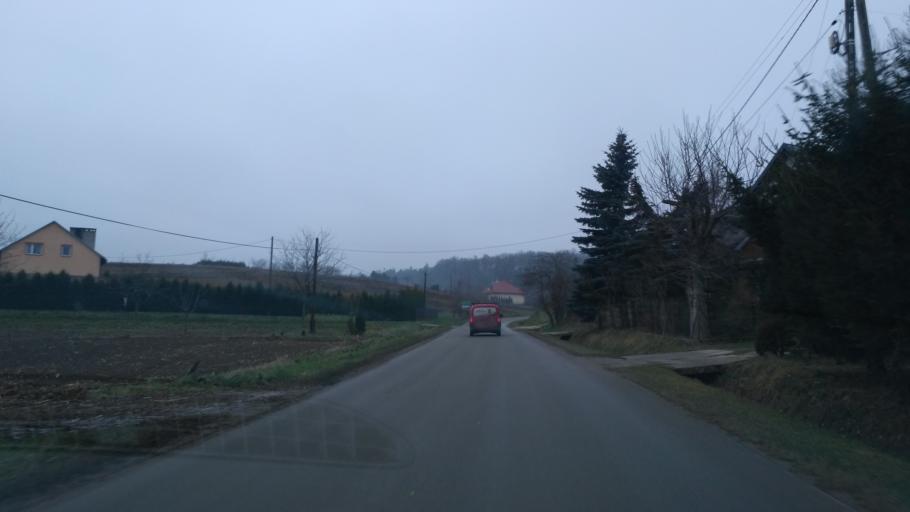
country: PL
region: Subcarpathian Voivodeship
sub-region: Powiat przeworski
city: Zarzecze
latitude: 49.9930
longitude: 22.5209
